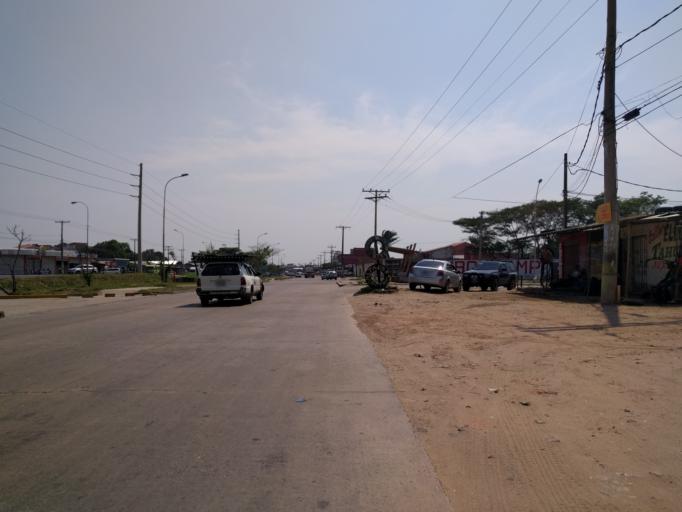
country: BO
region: Santa Cruz
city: Santa Cruz de la Sierra
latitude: -17.8047
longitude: -63.1529
